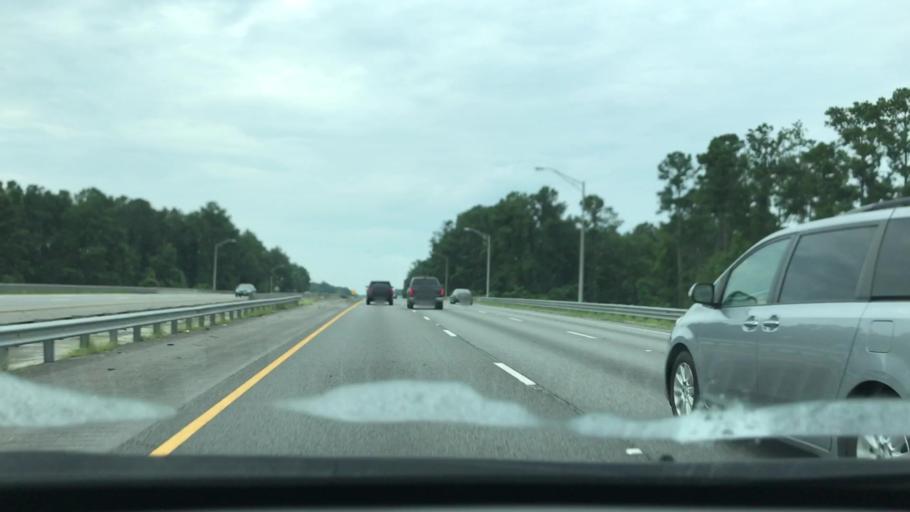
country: US
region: Georgia
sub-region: Bryan County
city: Richmond Hill
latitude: 31.9320
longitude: -81.3326
